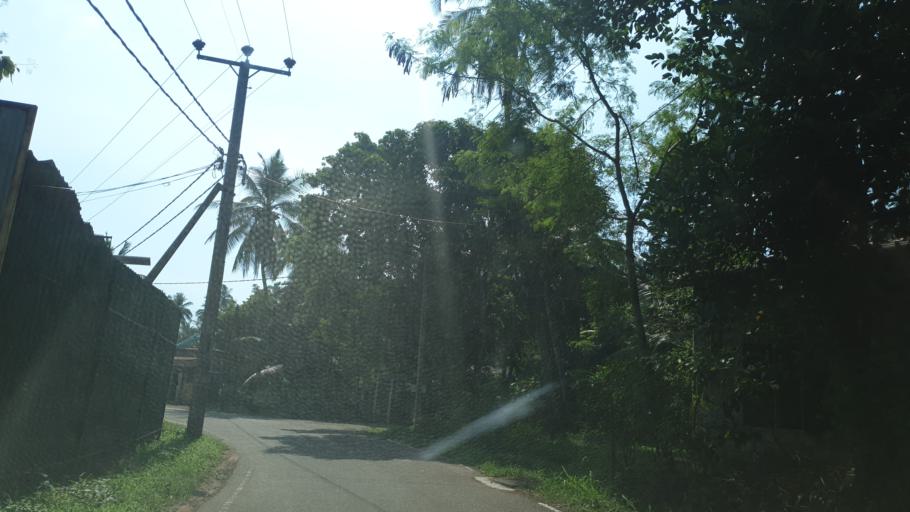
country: LK
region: Western
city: Moratuwa
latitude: 6.7624
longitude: 79.9283
